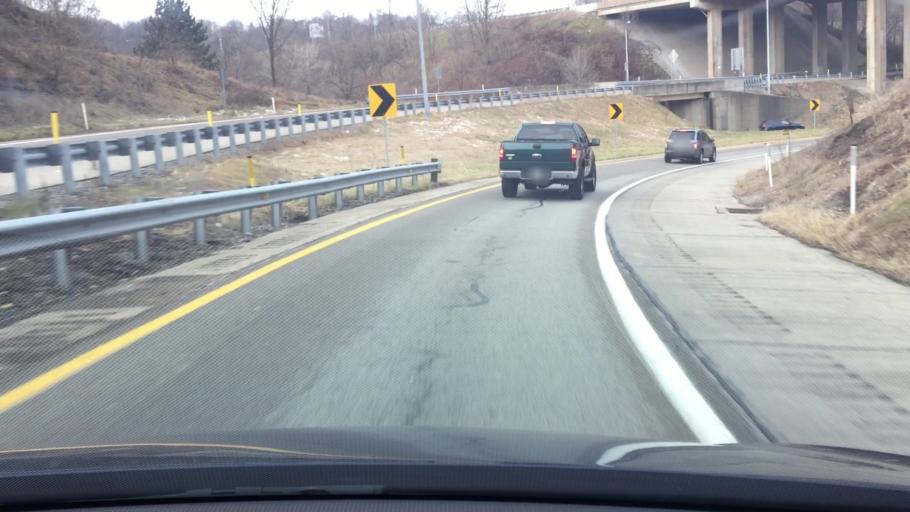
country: US
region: Pennsylvania
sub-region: Allegheny County
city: Churchill
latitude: 40.4409
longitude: -79.8271
